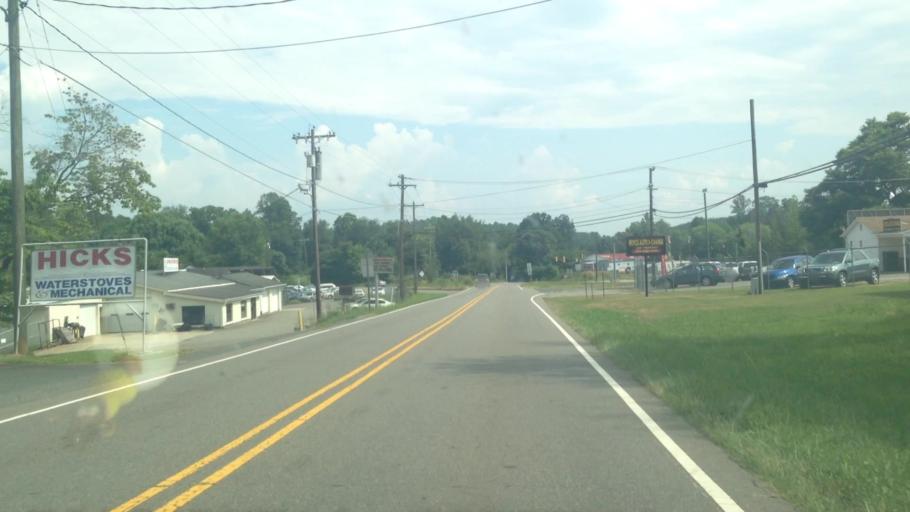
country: US
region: North Carolina
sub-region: Surry County
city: Flat Rock
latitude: 36.4725
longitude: -80.5739
